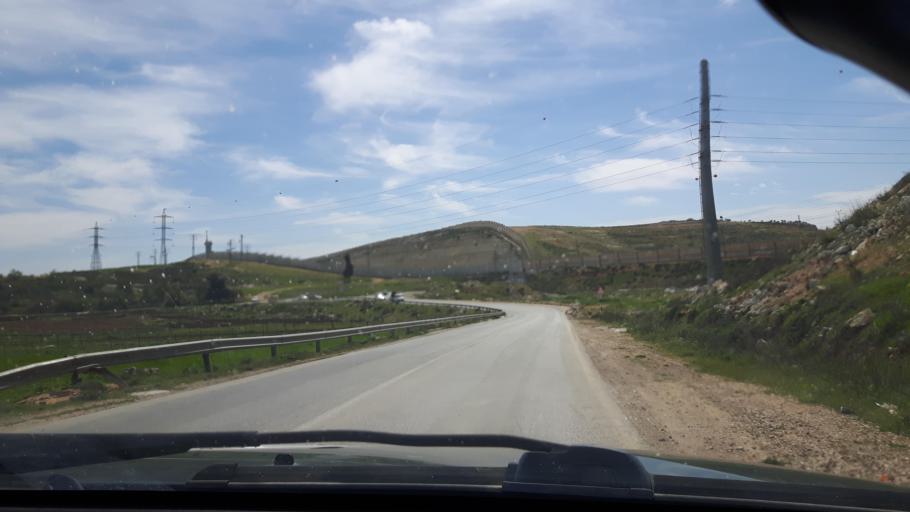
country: PS
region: West Bank
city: Qalandiya
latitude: 31.8629
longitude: 35.2033
